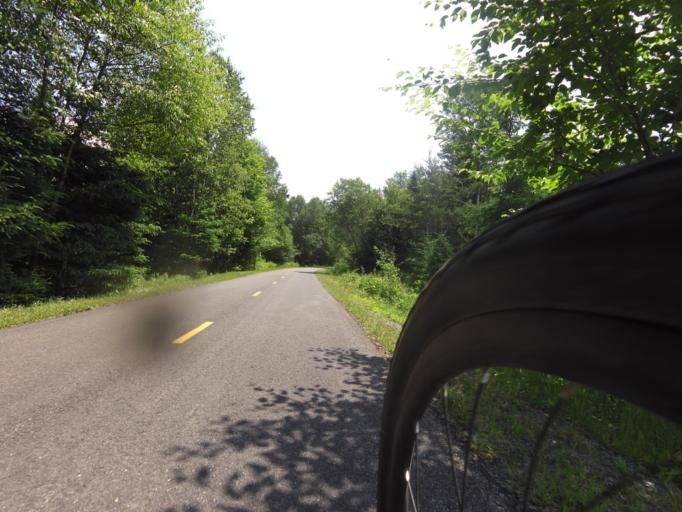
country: CA
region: Quebec
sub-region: Laurentides
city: Mont-Tremblant
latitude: 46.1537
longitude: -74.5963
